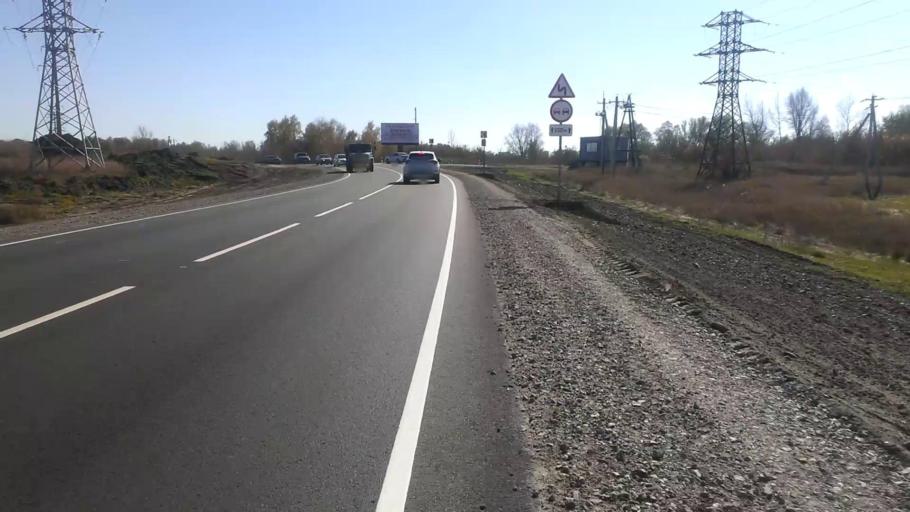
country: RU
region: Altai Krai
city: Sannikovo
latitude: 53.3300
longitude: 83.9387
